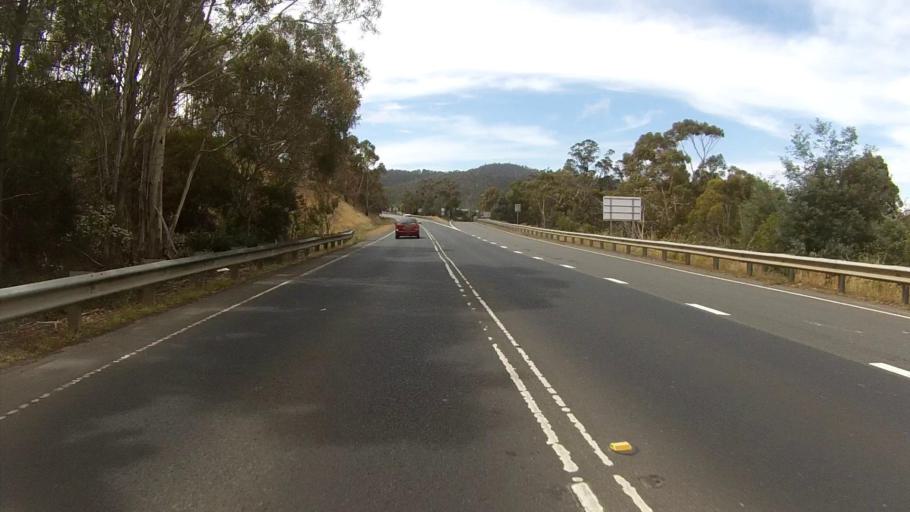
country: AU
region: Tasmania
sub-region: Kingborough
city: Kingston
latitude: -42.9724
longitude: 147.3070
